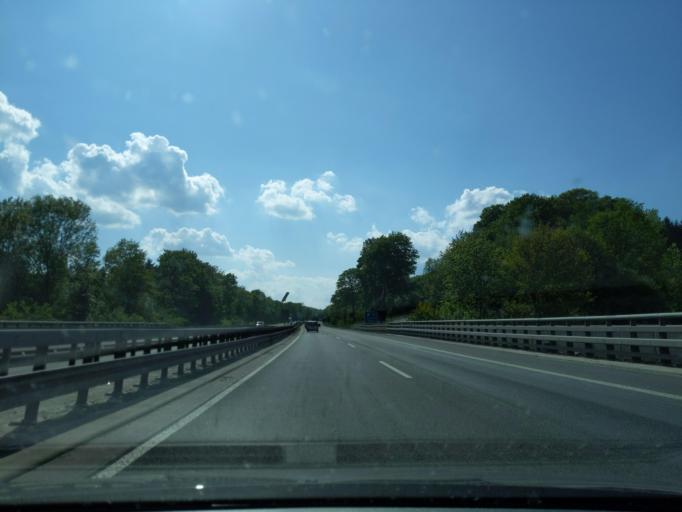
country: DE
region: North Rhine-Westphalia
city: Wiehl
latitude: 50.9753
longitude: 7.4851
